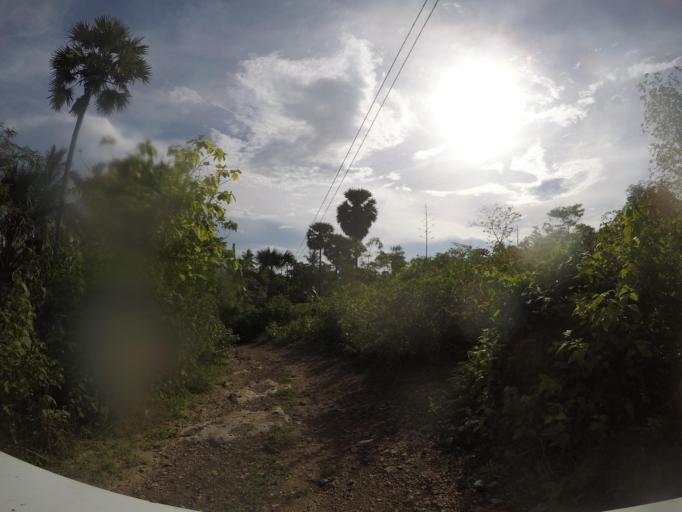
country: TL
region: Baucau
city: Baucau
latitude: -8.5053
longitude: 126.4481
